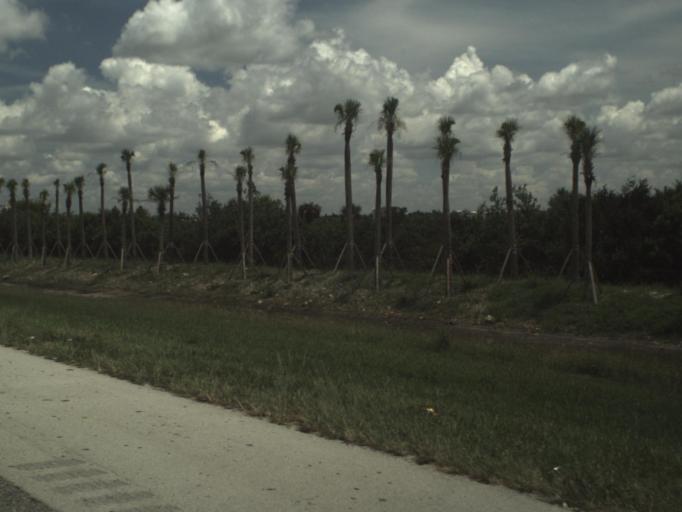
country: US
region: Florida
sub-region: Broward County
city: Sunshine Ranches
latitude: 26.0203
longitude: -80.3467
